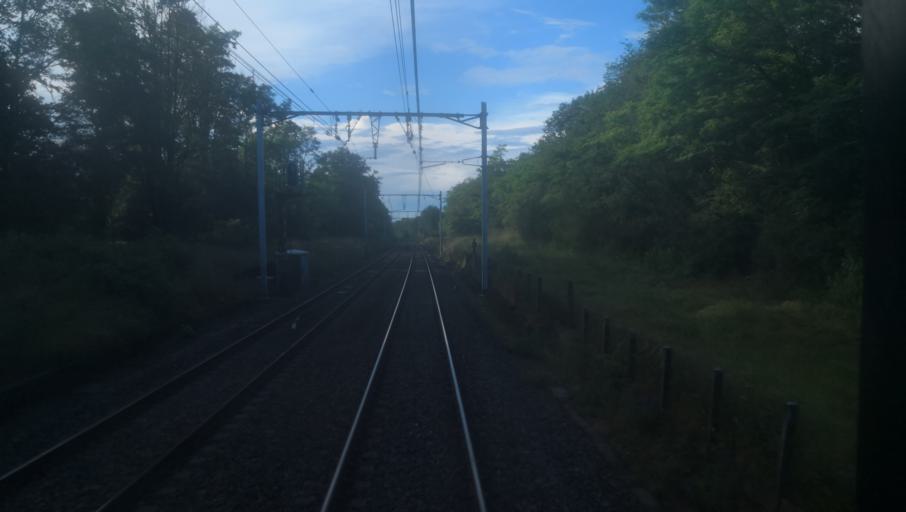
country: FR
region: Centre
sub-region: Departement du Loir-et-Cher
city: Salbris
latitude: 47.3980
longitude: 2.0519
